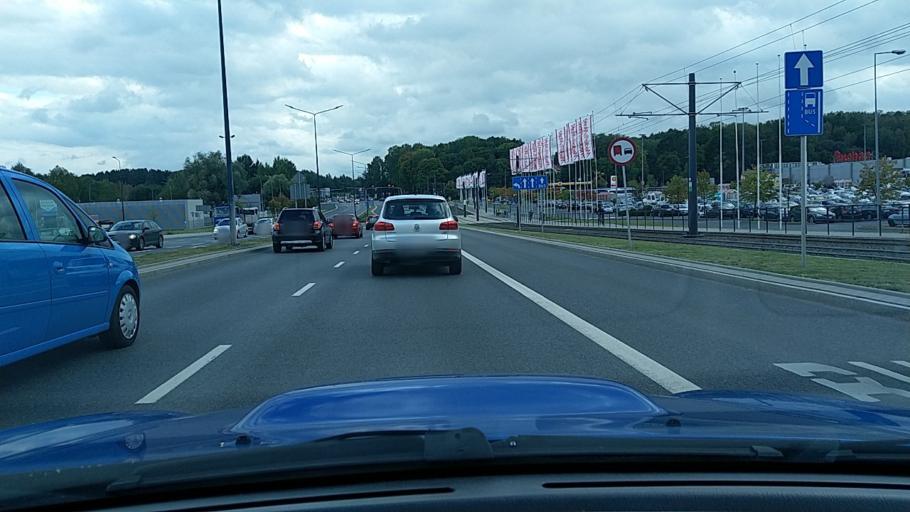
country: PL
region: Warmian-Masurian Voivodeship
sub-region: Powiat olsztynski
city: Olsztyn
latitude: 53.7525
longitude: 20.4861
